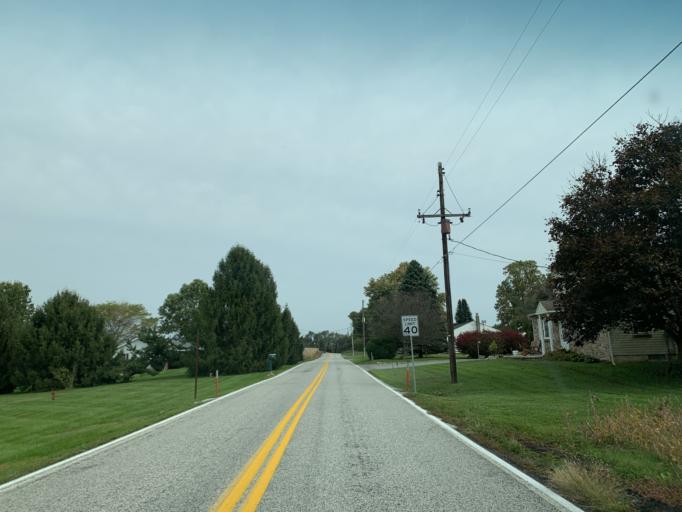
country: US
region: Pennsylvania
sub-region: York County
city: Susquehanna Trails
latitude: 39.7419
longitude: -76.4463
